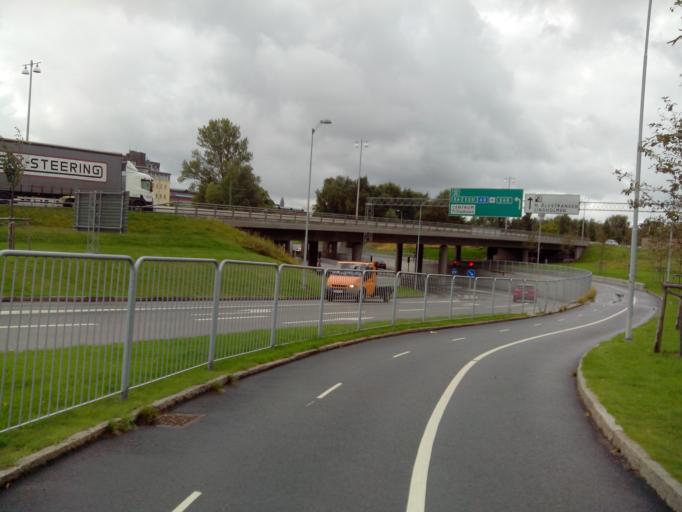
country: SE
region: Vaestra Goetaland
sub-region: Goteborg
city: Goeteborg
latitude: 57.7140
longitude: 11.9440
